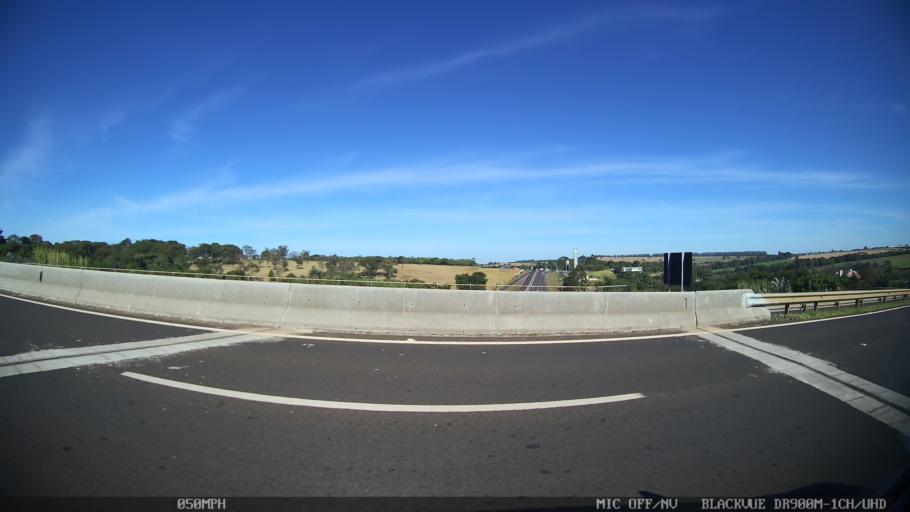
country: BR
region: Sao Paulo
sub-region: Franca
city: Franca
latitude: -20.5611
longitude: -47.4135
